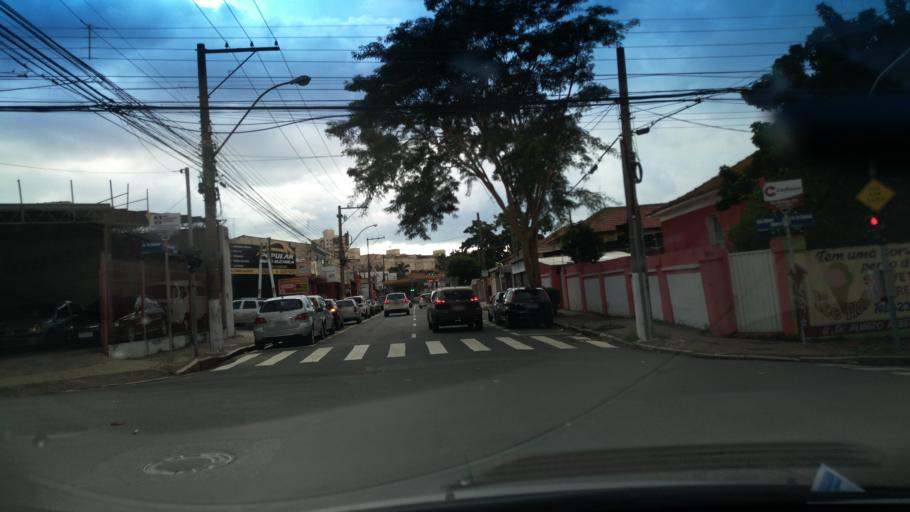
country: BR
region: Sao Paulo
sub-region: Campinas
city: Campinas
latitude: -22.9158
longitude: -47.0558
